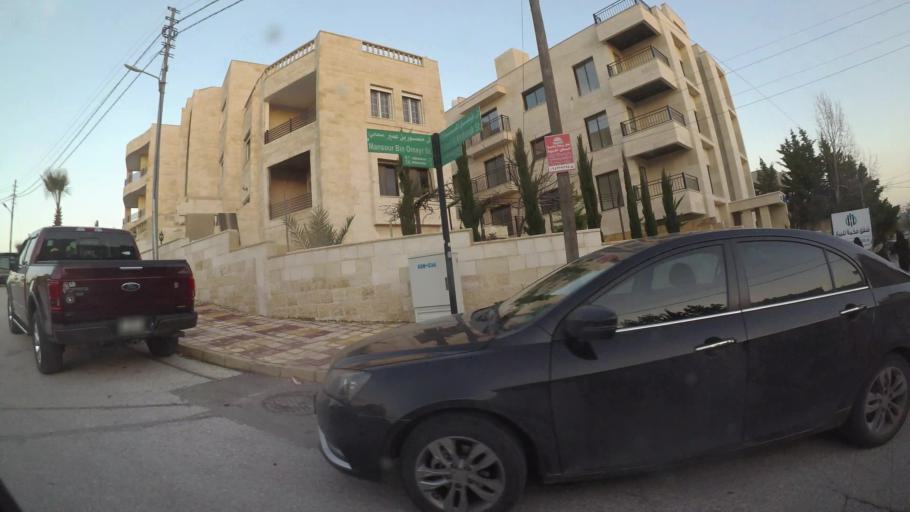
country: JO
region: Amman
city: Al Jubayhah
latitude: 32.0019
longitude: 35.8521
